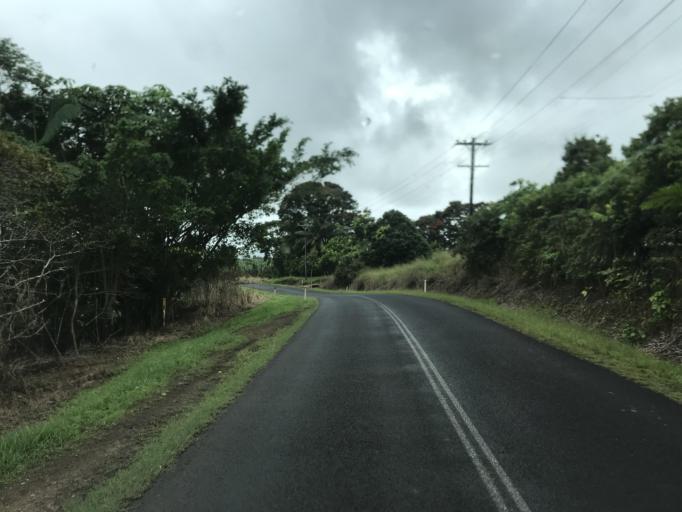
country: AU
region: Queensland
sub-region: Cassowary Coast
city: Innisfail
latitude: -17.5163
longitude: 145.9746
